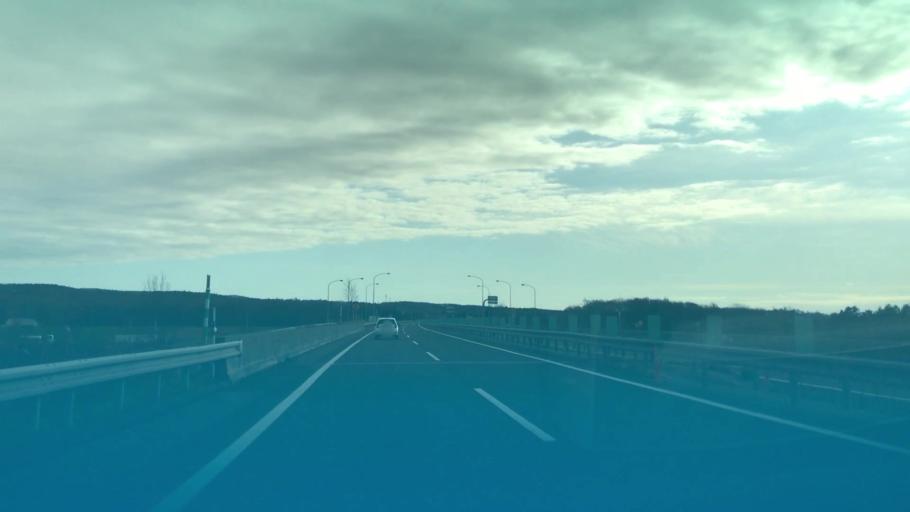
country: JP
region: Hokkaido
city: Chitose
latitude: 42.8823
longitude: 141.7110
